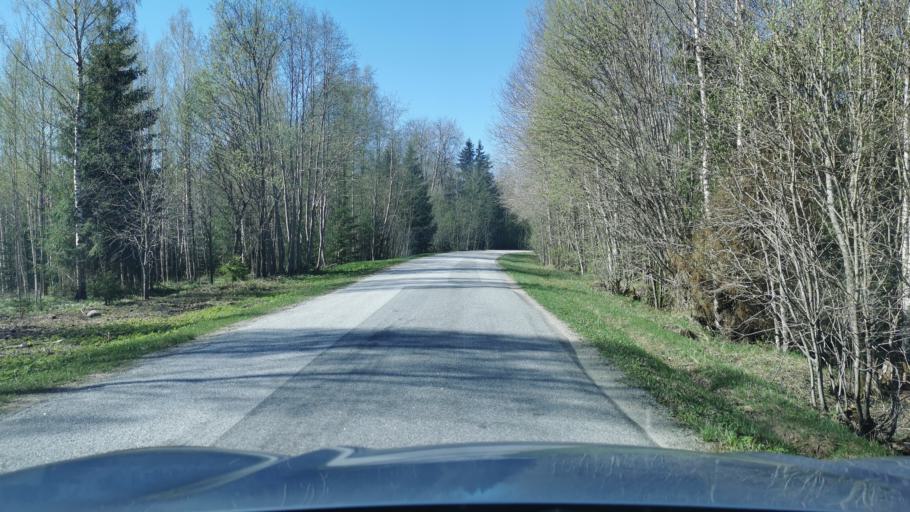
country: EE
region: Jogevamaa
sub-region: Mustvee linn
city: Mustvee
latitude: 59.0424
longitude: 26.6605
